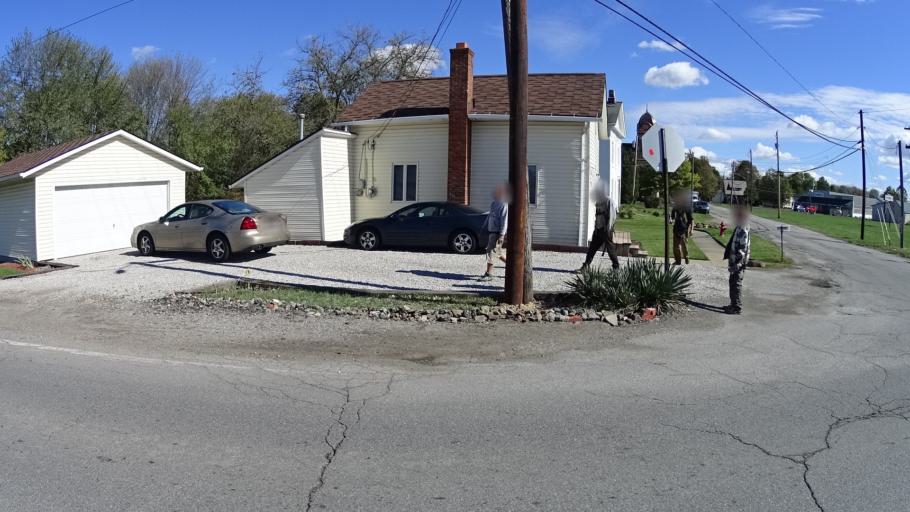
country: US
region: Ohio
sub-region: Lorain County
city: Grafton
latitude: 41.2768
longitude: -82.0617
